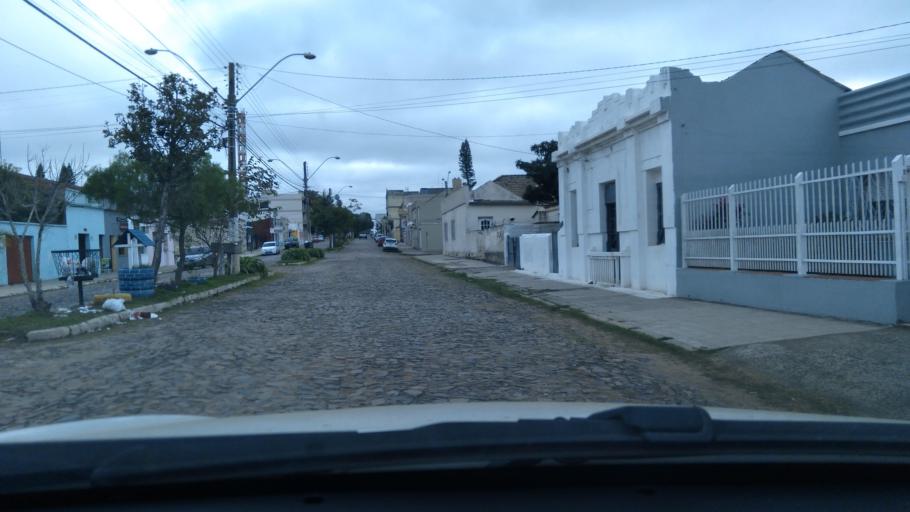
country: BR
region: Rio Grande do Sul
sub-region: Dom Pedrito
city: Dom Pedrito
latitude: -30.9856
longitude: -54.6693
